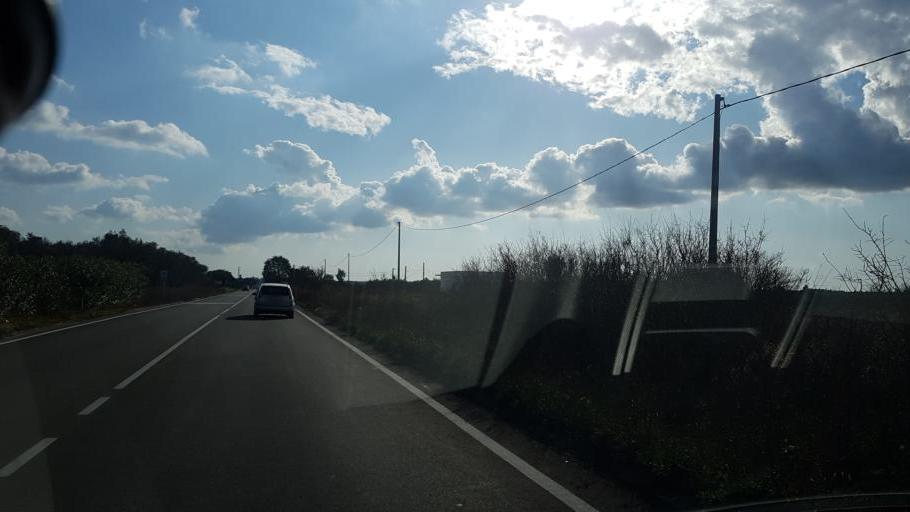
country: IT
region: Apulia
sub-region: Provincia di Lecce
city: Salice Salentino
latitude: 40.3631
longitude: 17.9676
